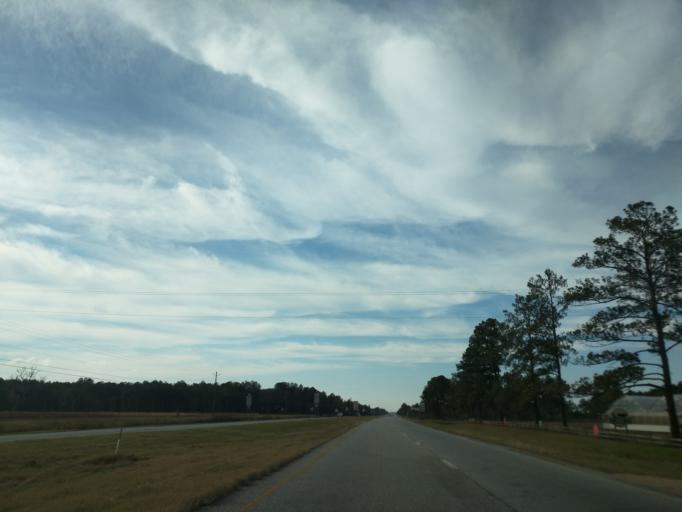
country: US
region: Georgia
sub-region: Decatur County
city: Bainbridge
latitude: 30.8893
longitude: -84.4840
